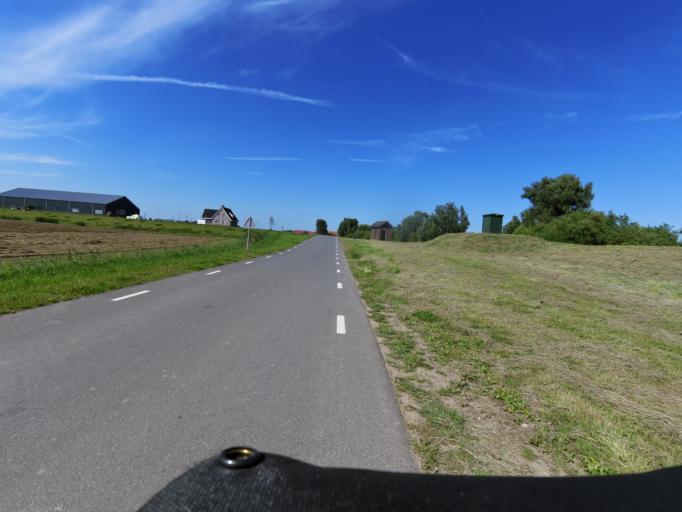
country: NL
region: North Brabant
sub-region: Gemeente Werkendam
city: Werkendam
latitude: 51.7665
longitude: 4.8584
